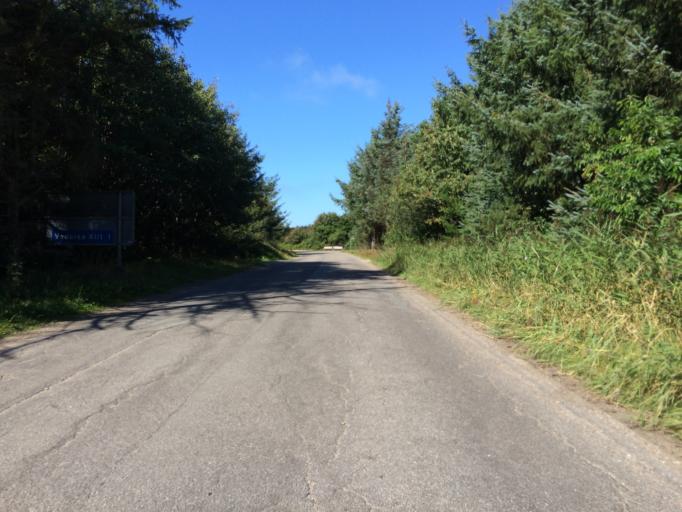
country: DK
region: Central Jutland
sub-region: Holstebro Kommune
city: Ulfborg
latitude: 56.2595
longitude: 8.1485
